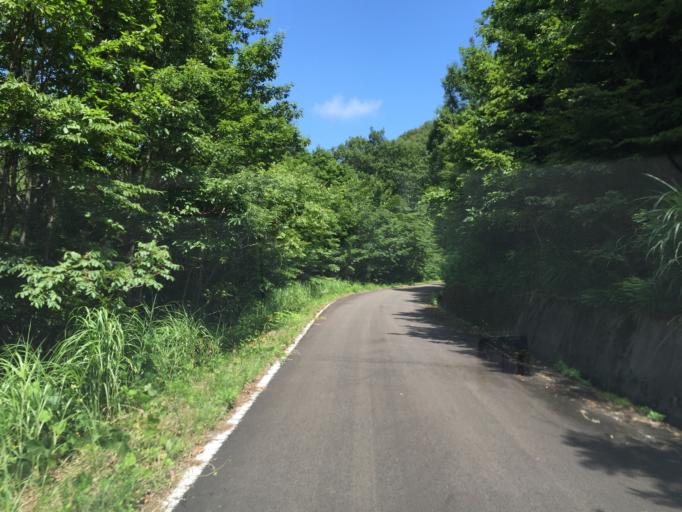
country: JP
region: Fukushima
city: Inawashiro
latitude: 37.4332
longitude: 140.0613
